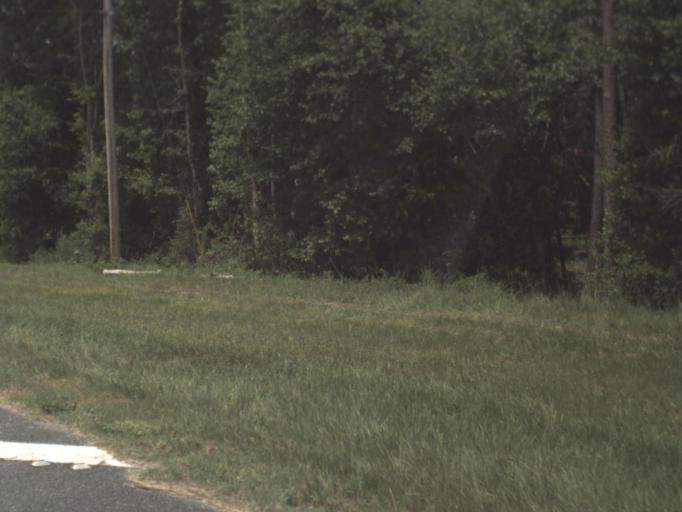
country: US
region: Florida
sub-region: Baker County
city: Macclenny
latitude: 30.3467
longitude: -82.1271
